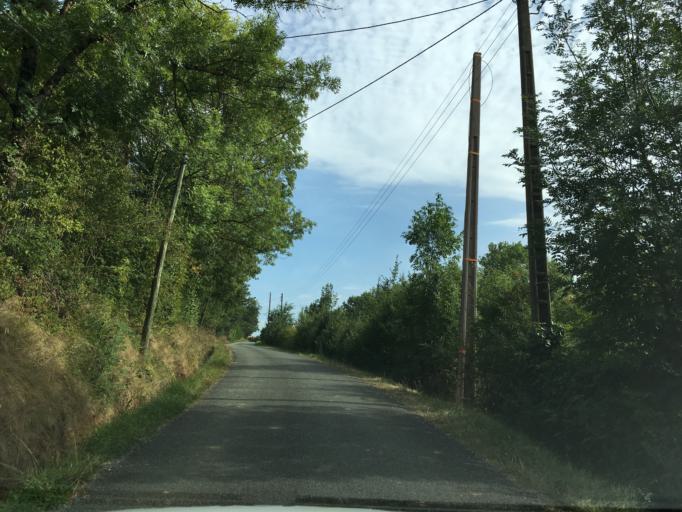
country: FR
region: Midi-Pyrenees
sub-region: Departement du Tarn
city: Castres
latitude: 43.6071
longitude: 2.2735
